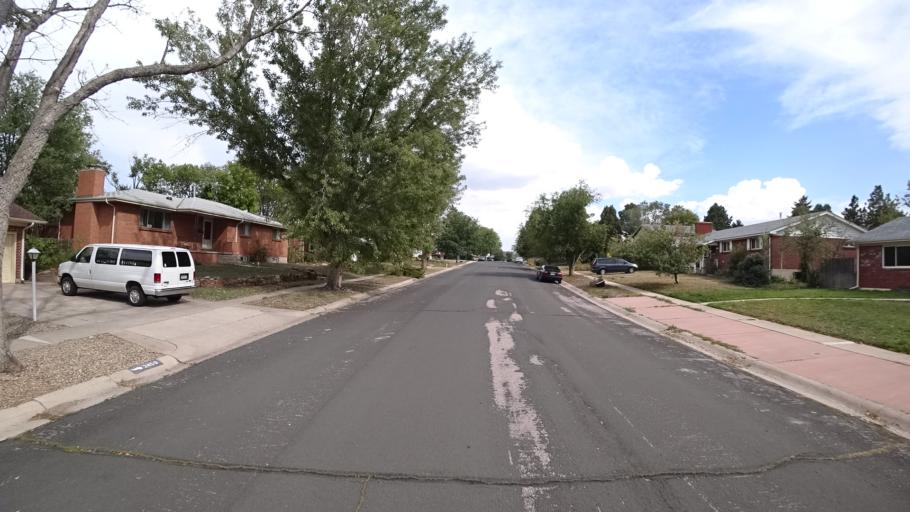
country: US
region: Colorado
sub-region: El Paso County
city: Colorado Springs
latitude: 38.8669
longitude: -104.7795
